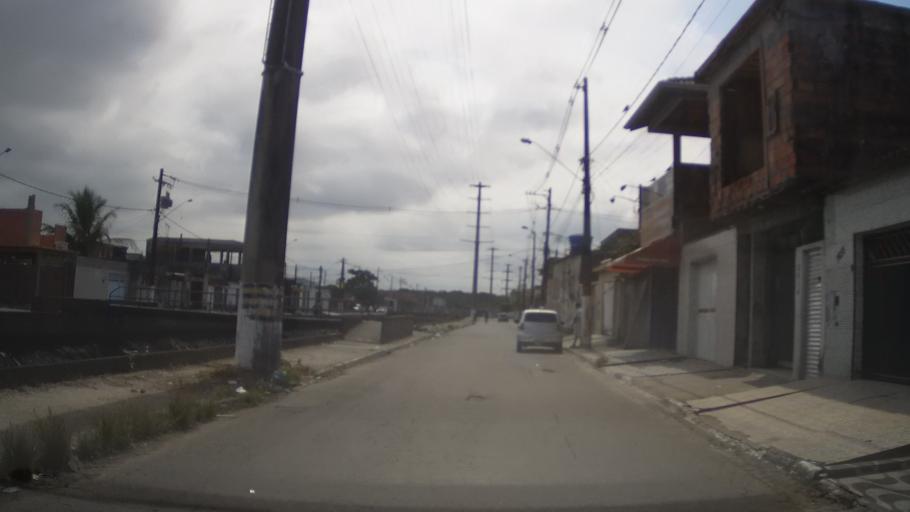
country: BR
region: Sao Paulo
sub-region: Praia Grande
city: Praia Grande
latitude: -24.0159
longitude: -46.4901
